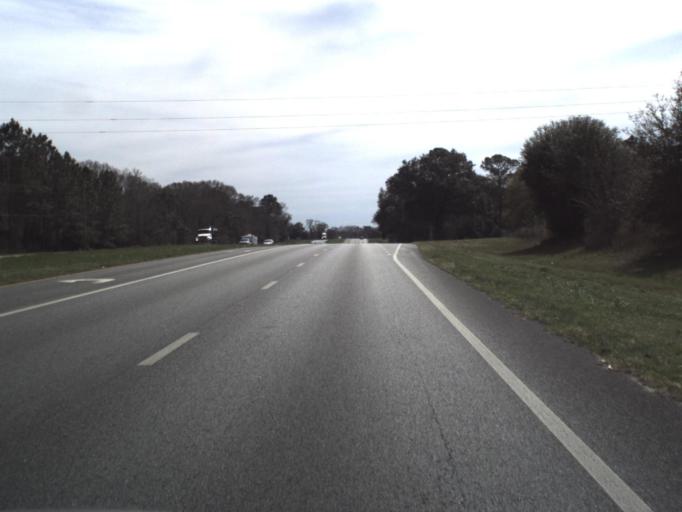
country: US
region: Florida
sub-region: Jackson County
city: Marianna
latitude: 30.7825
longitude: -85.3753
